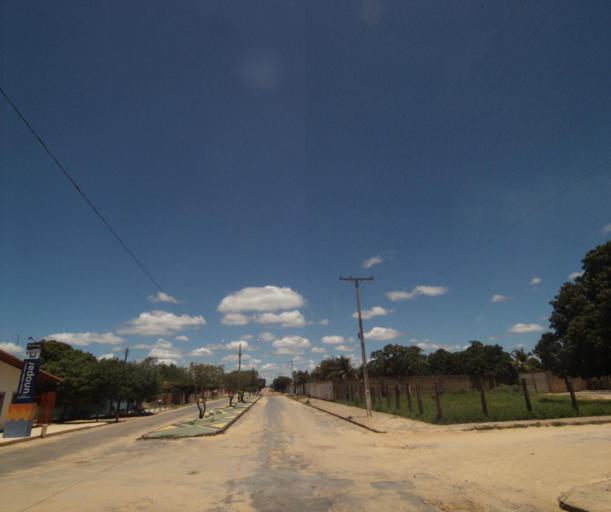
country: BR
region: Bahia
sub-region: Carinhanha
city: Carinhanha
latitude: -14.2956
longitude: -43.7742
